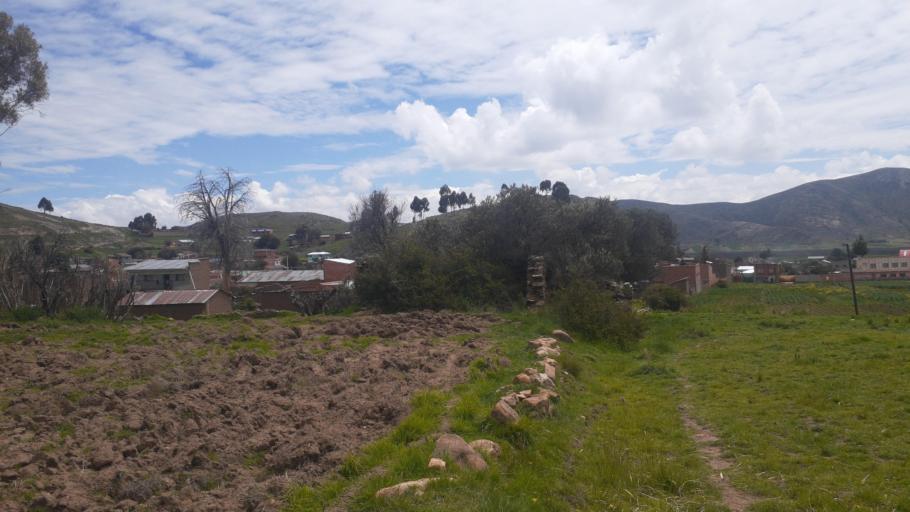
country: BO
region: La Paz
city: Batallas
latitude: -16.3482
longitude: -68.6395
